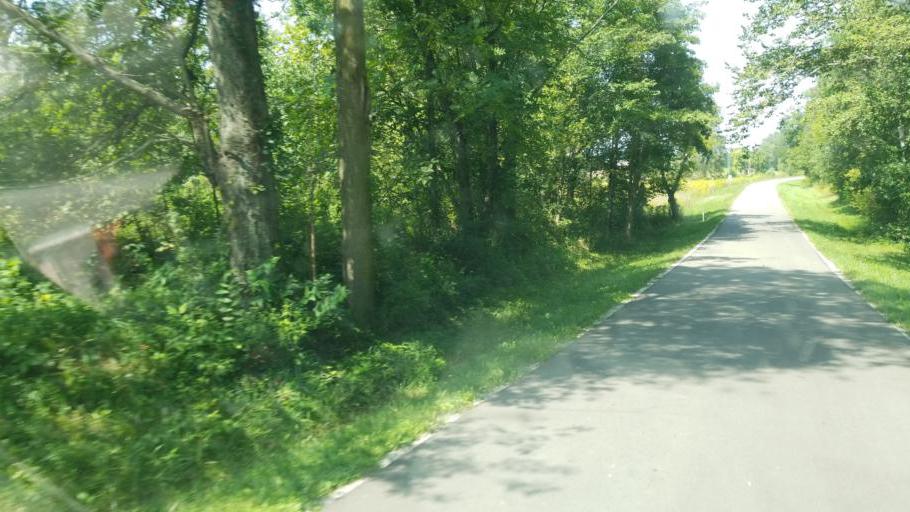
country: US
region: Ohio
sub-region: Crawford County
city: Bucyrus
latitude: 40.9279
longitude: -83.0742
